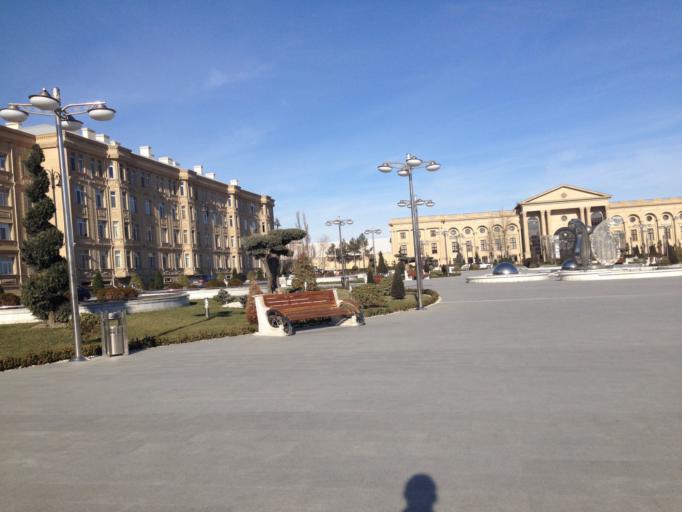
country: AZ
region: Baki
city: Baku
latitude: 40.4045
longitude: 49.8564
